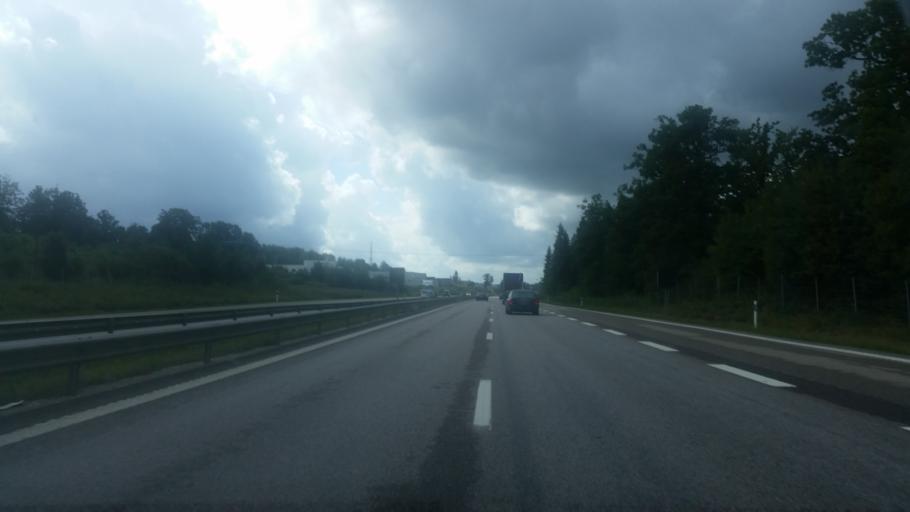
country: SE
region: Vaestra Goetaland
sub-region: Boras Kommun
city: Sjomarken
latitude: 57.7067
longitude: 12.8414
